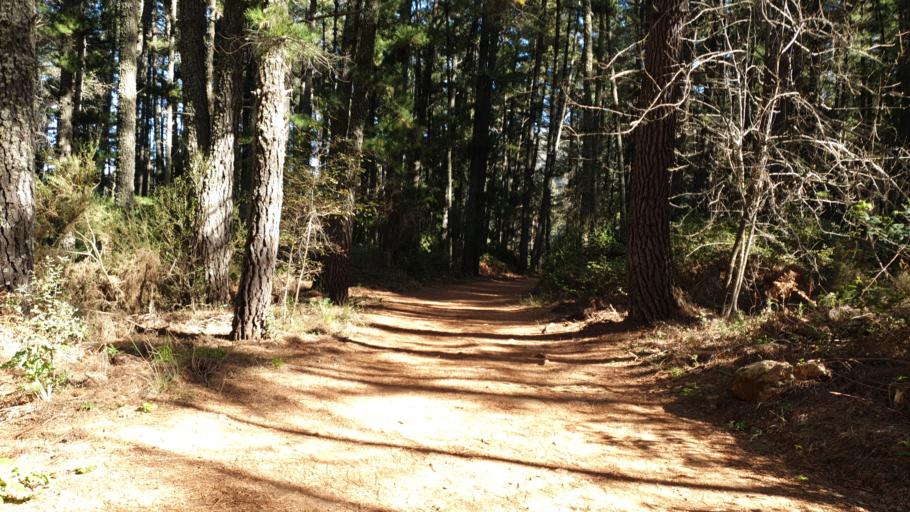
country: ES
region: Andalusia
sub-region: Provincia de Malaga
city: Ojen
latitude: 36.5723
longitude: -4.8929
